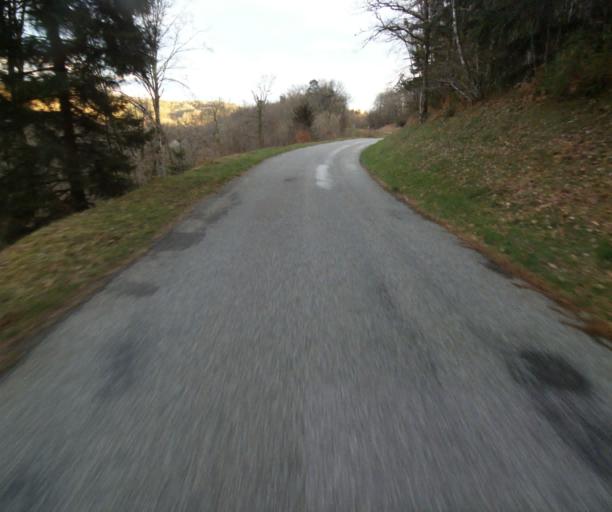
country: FR
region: Limousin
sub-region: Departement de la Correze
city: Argentat
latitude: 45.2506
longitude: 1.9837
